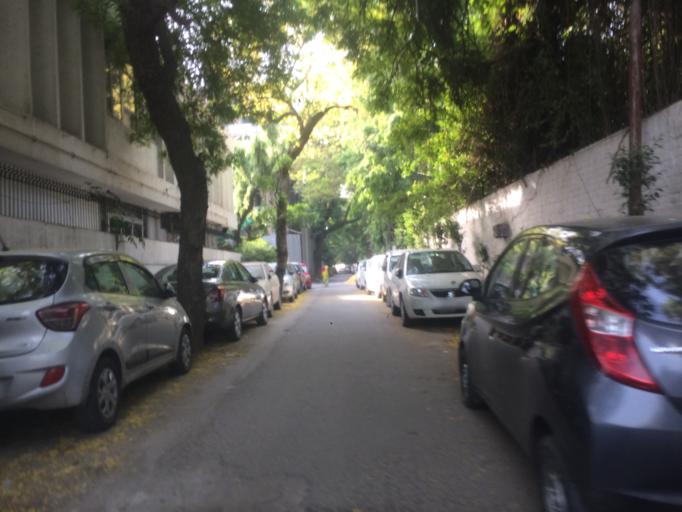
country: IN
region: NCT
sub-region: New Delhi
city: New Delhi
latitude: 28.5479
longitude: 77.2315
